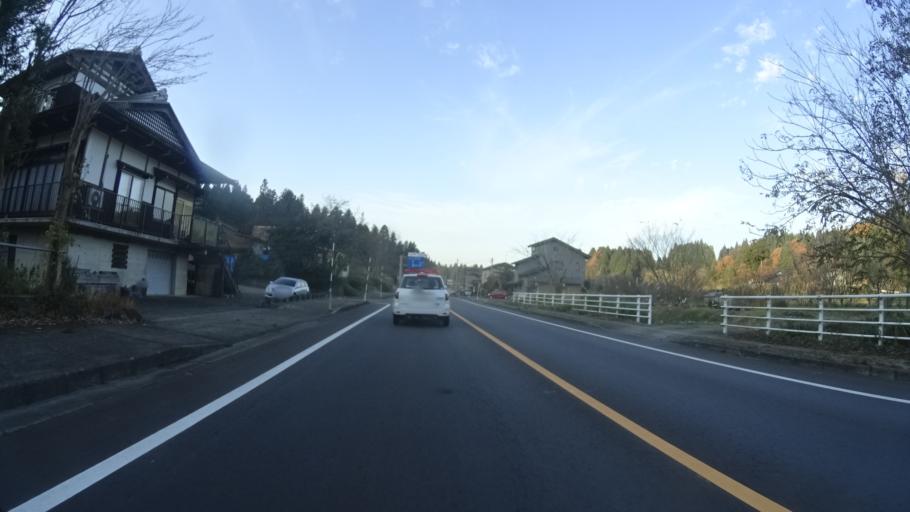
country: JP
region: Niigata
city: Nagaoka
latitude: 37.4247
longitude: 138.7262
